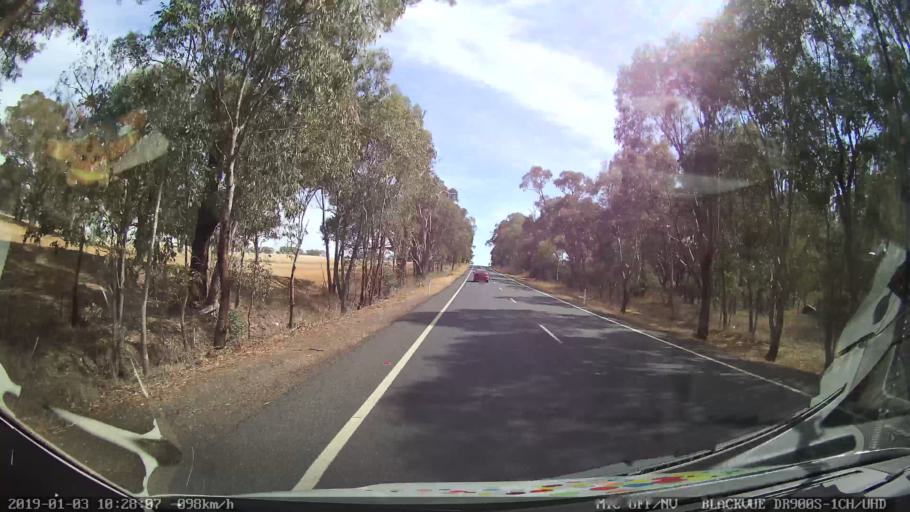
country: AU
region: New South Wales
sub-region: Young
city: Young
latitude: -34.3923
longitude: 148.2586
